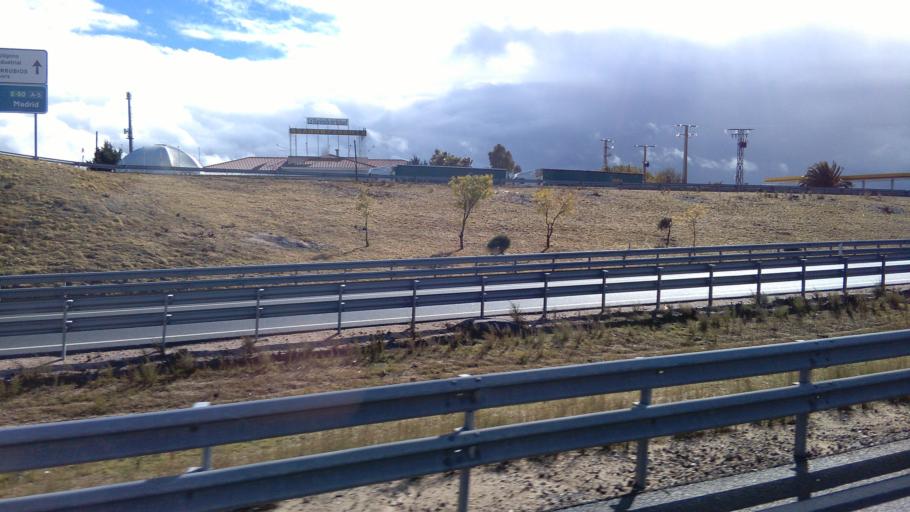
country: ES
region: Castille-La Mancha
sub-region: Province of Toledo
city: Valmojado
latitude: 40.2462
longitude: -4.0578
